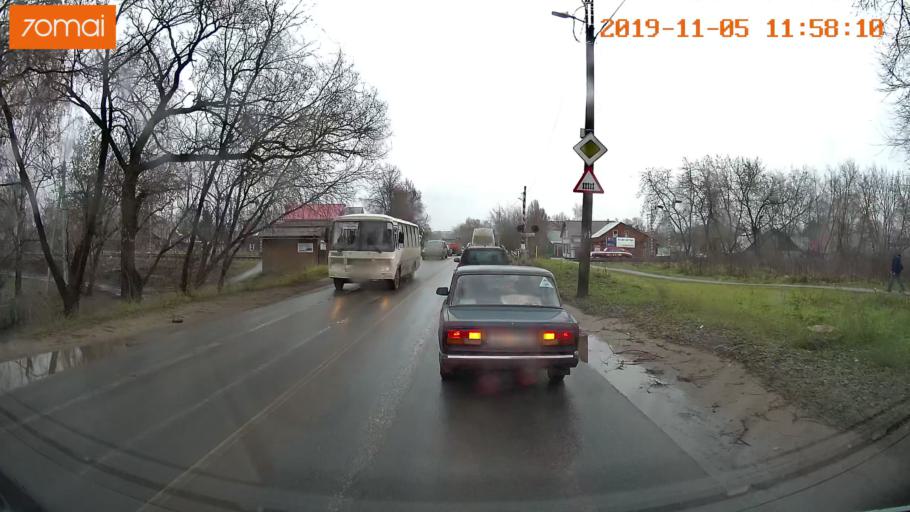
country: RU
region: Ivanovo
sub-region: Gorod Ivanovo
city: Ivanovo
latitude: 56.9813
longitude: 41.0391
